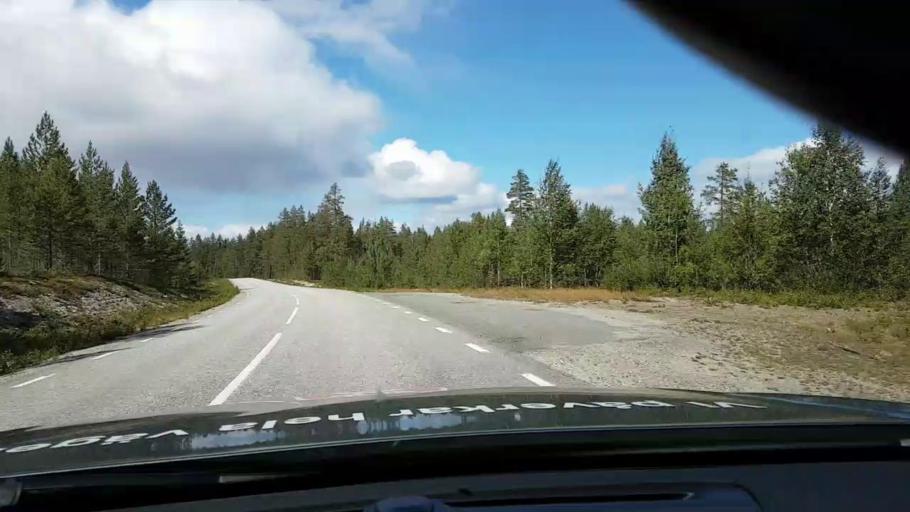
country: SE
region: Vaesternorrland
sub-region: OErnskoeldsviks Kommun
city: Bredbyn
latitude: 63.6714
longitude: 17.8238
